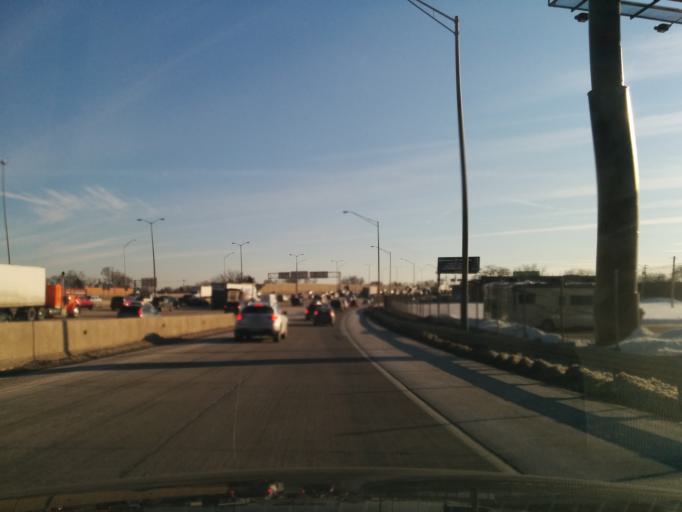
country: US
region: Illinois
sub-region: Cook County
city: Schiller Park
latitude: 41.9754
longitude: -87.8696
